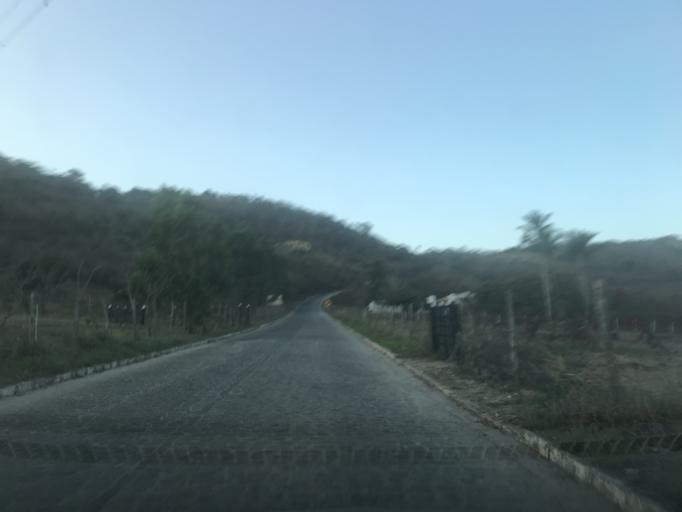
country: BR
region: Pernambuco
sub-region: Bezerros
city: Bezerros
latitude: -8.1880
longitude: -35.7615
